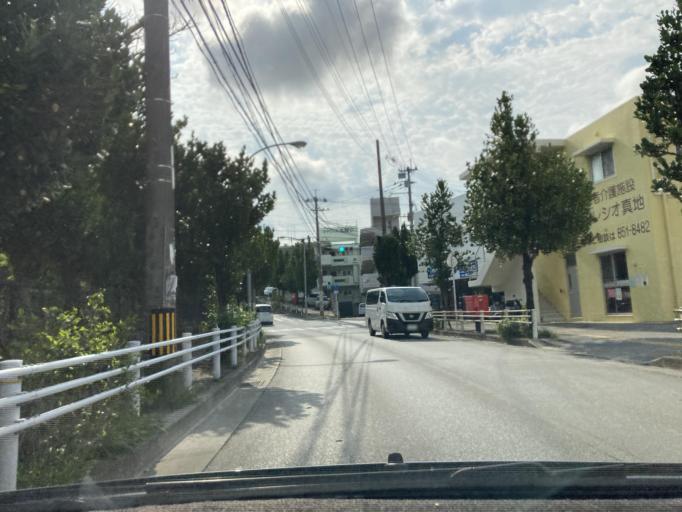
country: JP
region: Okinawa
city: Tomigusuku
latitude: 26.1993
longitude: 127.7181
